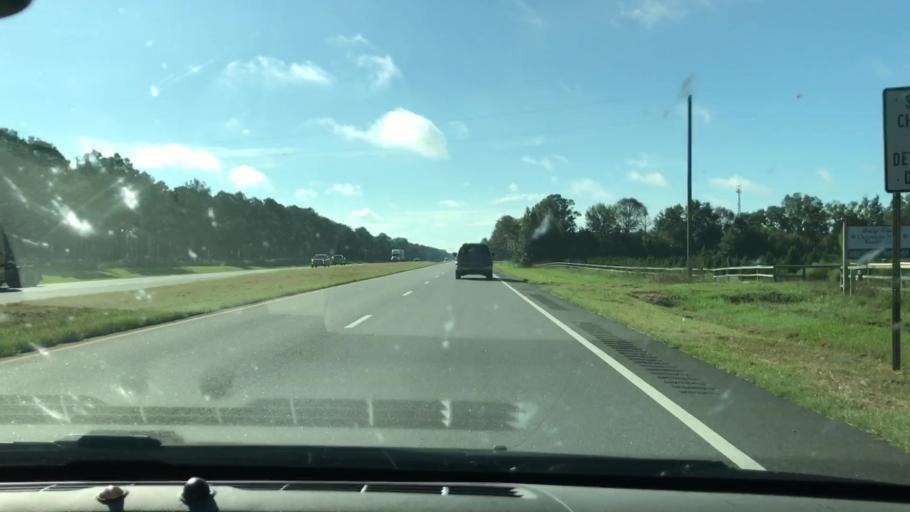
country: US
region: Georgia
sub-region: Lee County
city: Leesburg
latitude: 31.6911
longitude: -84.3128
